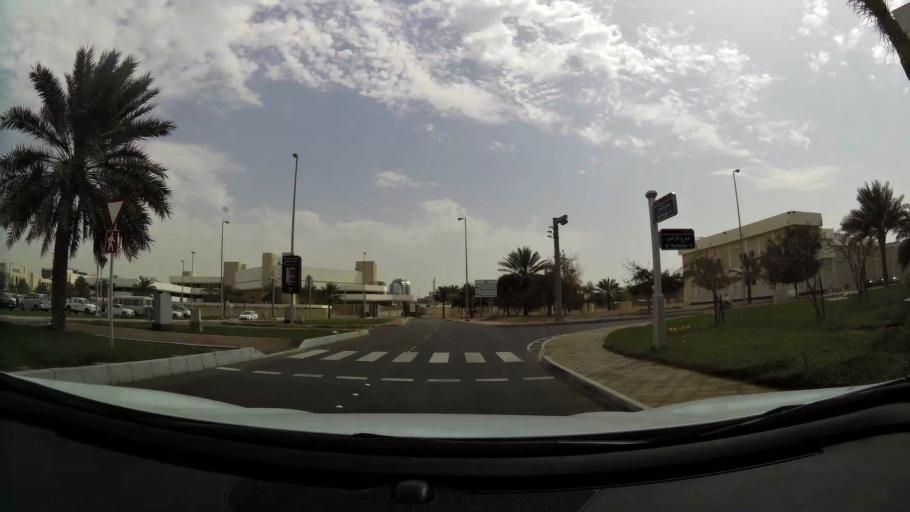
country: AE
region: Abu Dhabi
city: Abu Dhabi
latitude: 24.4645
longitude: 54.3301
